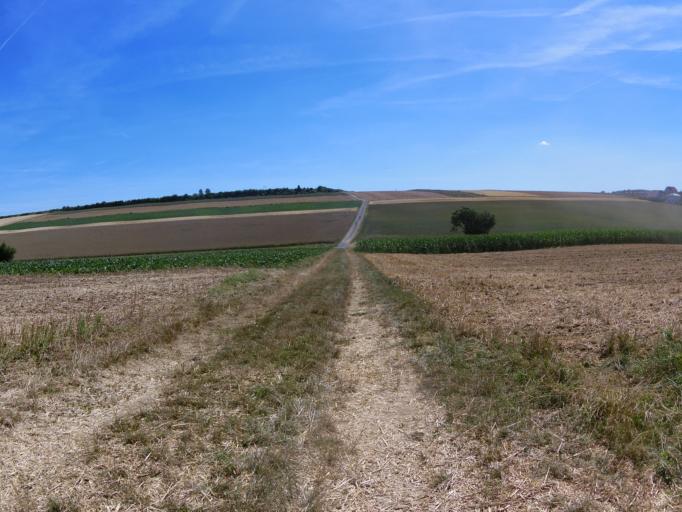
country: DE
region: Bavaria
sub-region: Regierungsbezirk Unterfranken
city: Hettstadt
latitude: 49.8032
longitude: 9.8324
